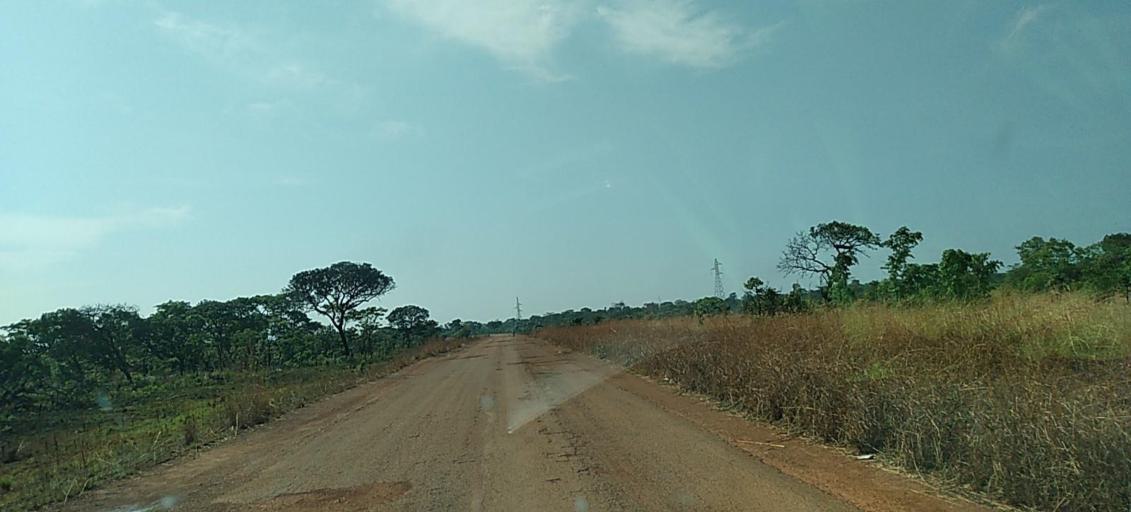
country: ZM
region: North-Western
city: Mwinilunga
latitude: -11.7824
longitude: 25.0243
